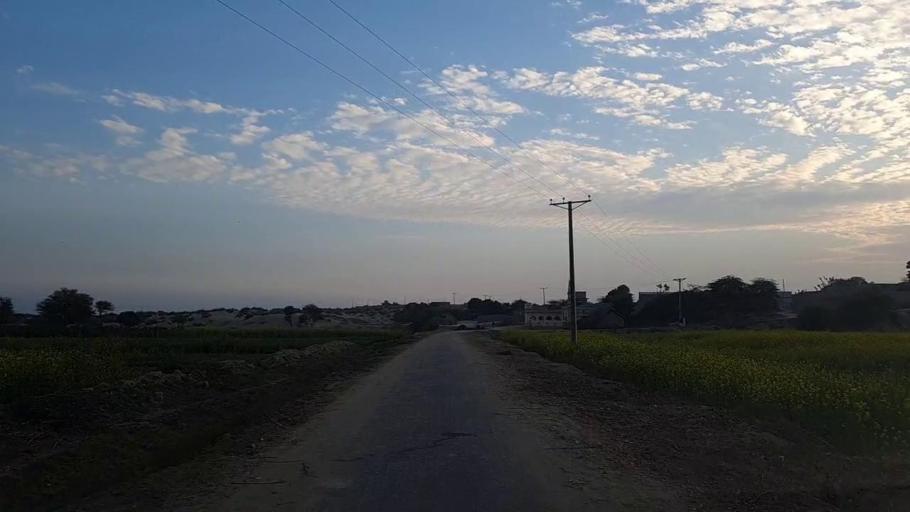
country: PK
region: Sindh
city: Daur
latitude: 26.4138
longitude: 68.4678
